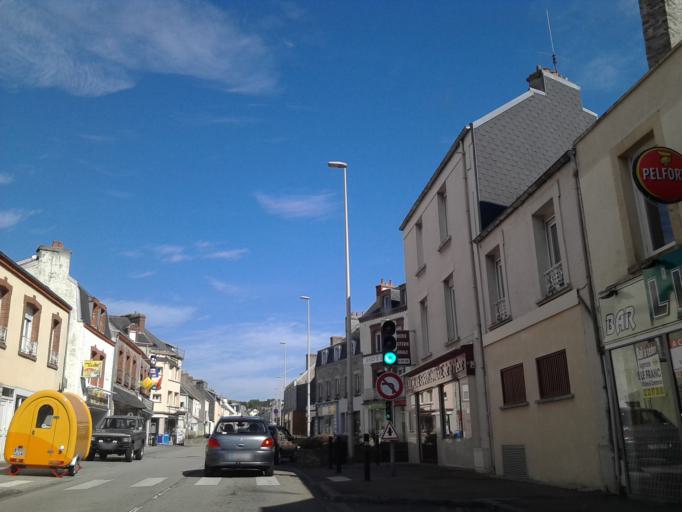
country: FR
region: Lower Normandy
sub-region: Departement de la Manche
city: Tourlaville
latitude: 49.6398
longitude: -1.5708
